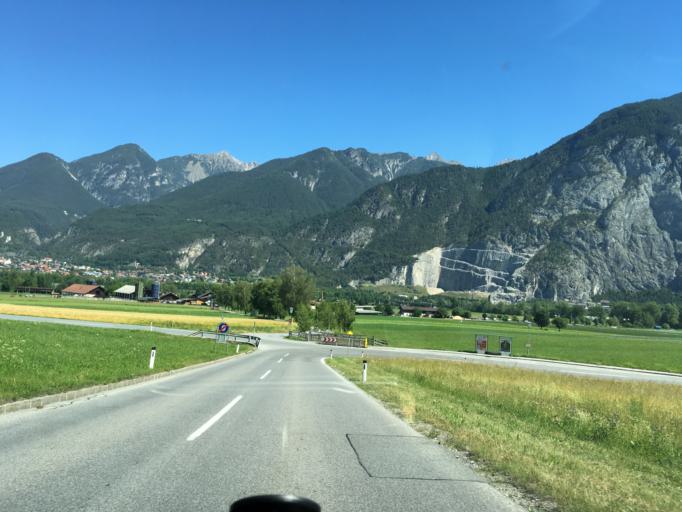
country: AT
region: Tyrol
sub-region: Politischer Bezirk Innsbruck Land
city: Kematen in Tirol
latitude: 47.2541
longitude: 11.2602
